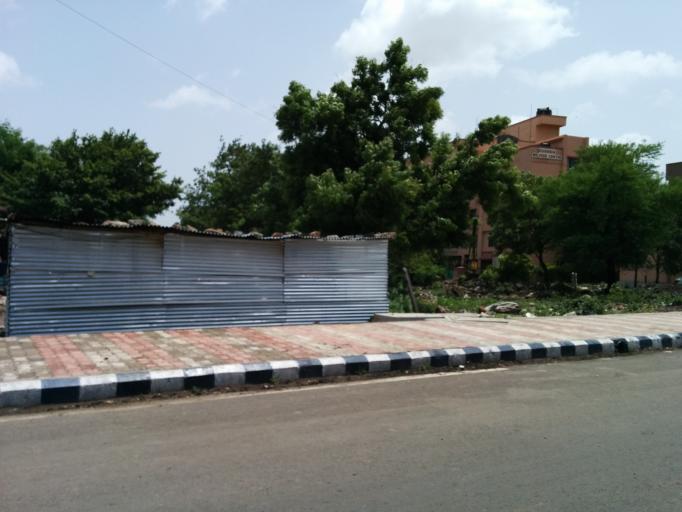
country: IN
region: Maharashtra
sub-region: Pune Division
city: Lohogaon
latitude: 18.5341
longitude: 73.9243
